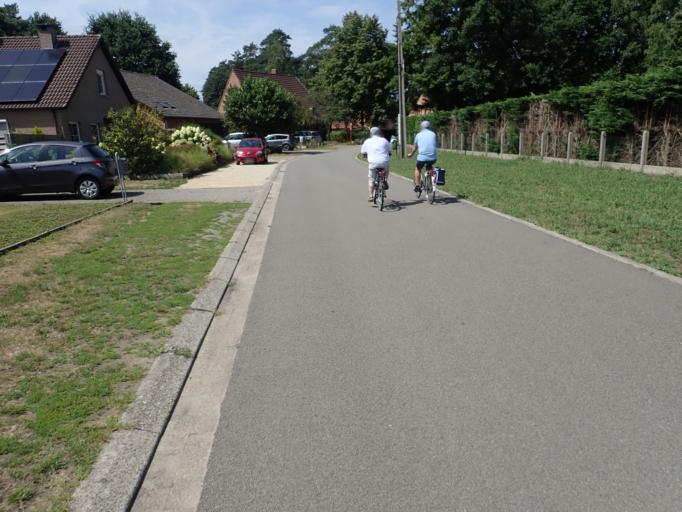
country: BE
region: Flanders
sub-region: Provincie Antwerpen
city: Zandhoven
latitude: 51.2179
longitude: 4.6603
